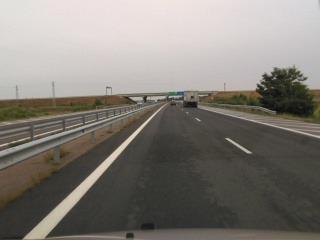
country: BG
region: Stara Zagora
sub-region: Obshtina Stara Zagora
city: Stara Zagora
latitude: 42.3387
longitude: 25.6589
